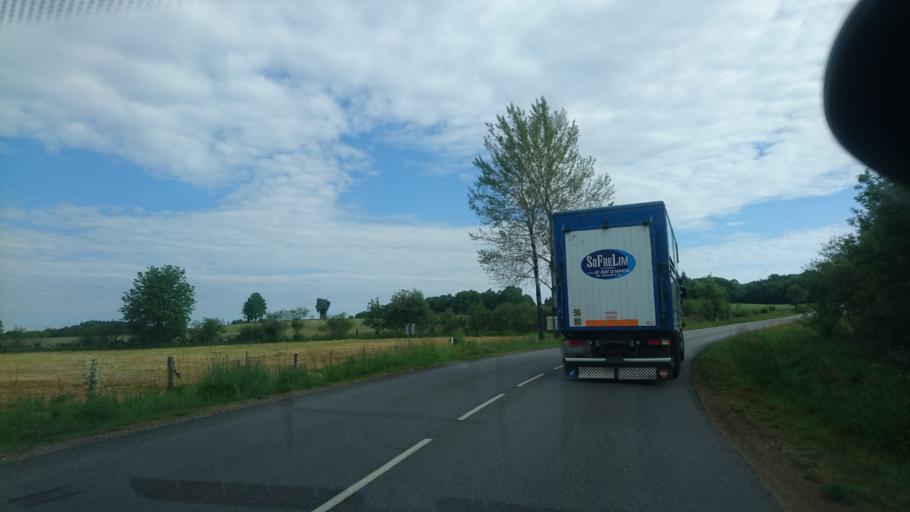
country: FR
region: Limousin
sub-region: Departement de la Haute-Vienne
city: Eymoutiers
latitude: 45.7638
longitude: 1.7497
